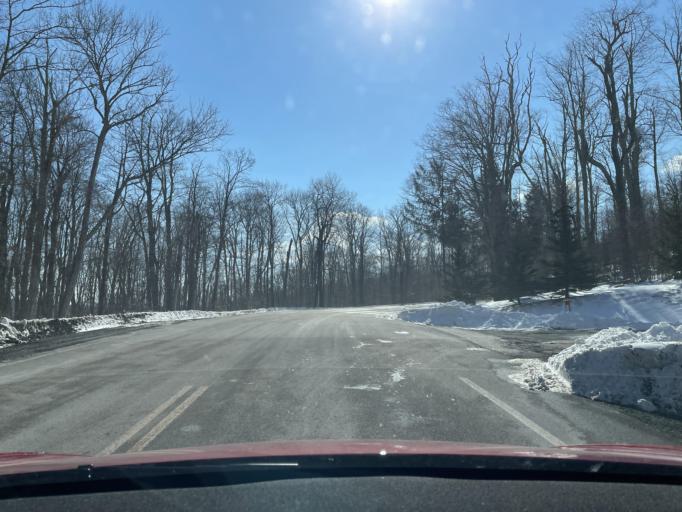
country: US
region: New York
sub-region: Delaware County
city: Stamford
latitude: 42.1370
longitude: -74.5097
